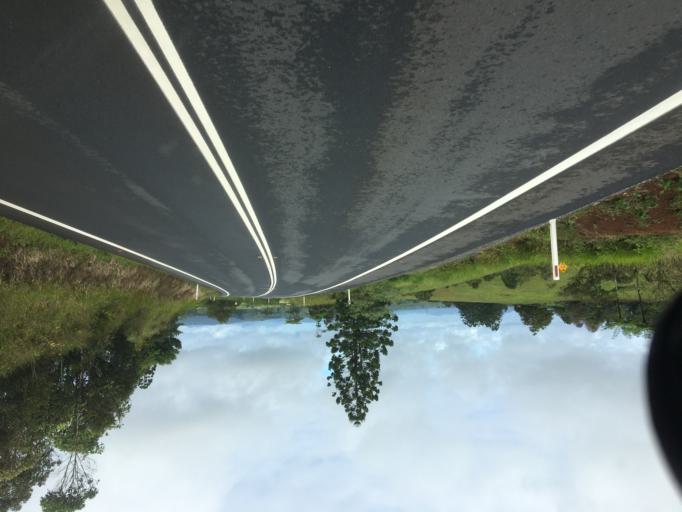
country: AU
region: Queensland
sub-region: Tablelands
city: Ravenshoe
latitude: -17.5054
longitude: 145.6304
